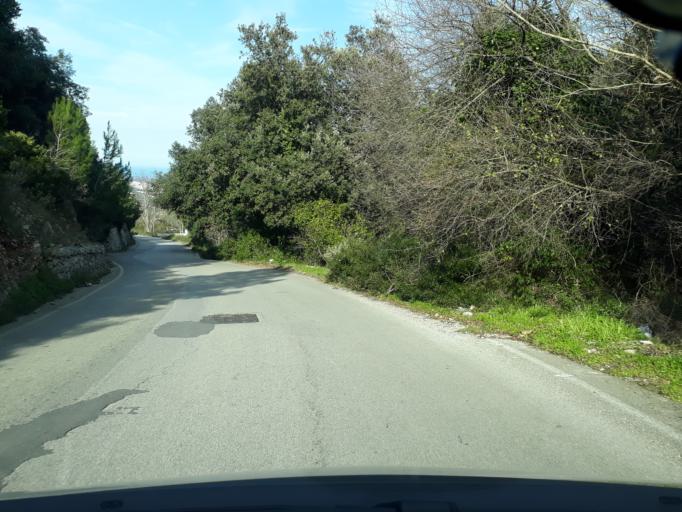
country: IT
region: Apulia
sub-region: Provincia di Brindisi
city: Lamie di Olimpie-Selva
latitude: 40.8043
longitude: 17.3523
